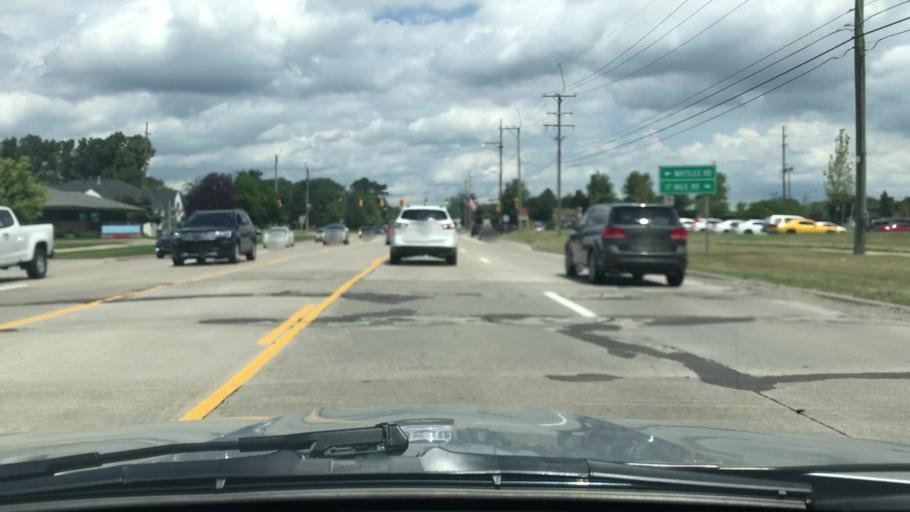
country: US
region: Michigan
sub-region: Macomb County
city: Sterling Heights
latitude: 42.5772
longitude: -83.0893
